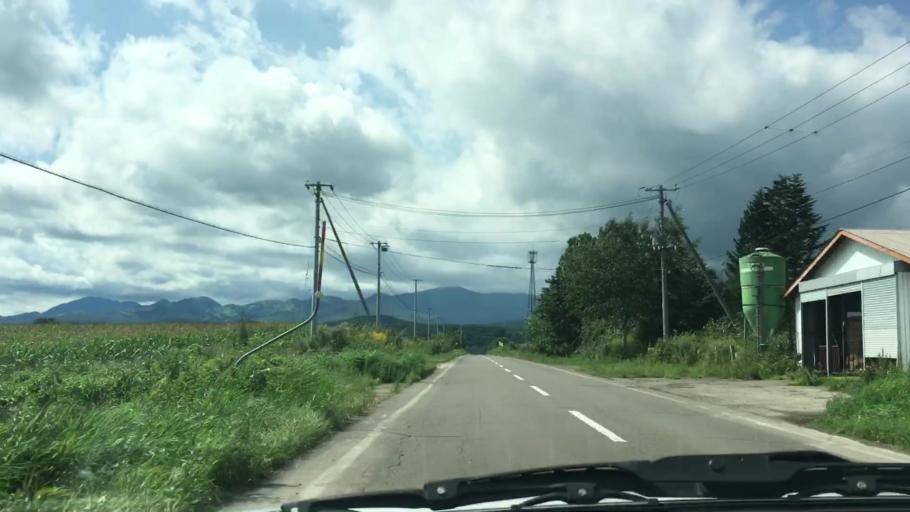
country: JP
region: Hokkaido
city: Otofuke
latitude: 43.2831
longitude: 143.3157
